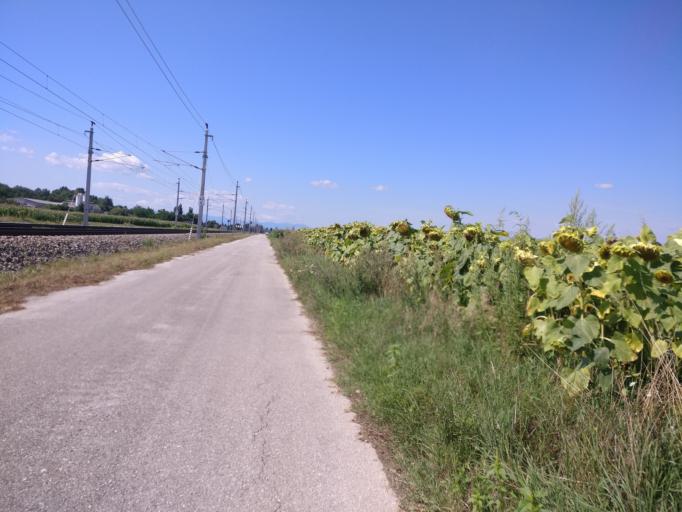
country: AT
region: Lower Austria
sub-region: Politischer Bezirk Wiener Neustadt
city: Zillingdorf
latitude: 47.8677
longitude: 16.3325
